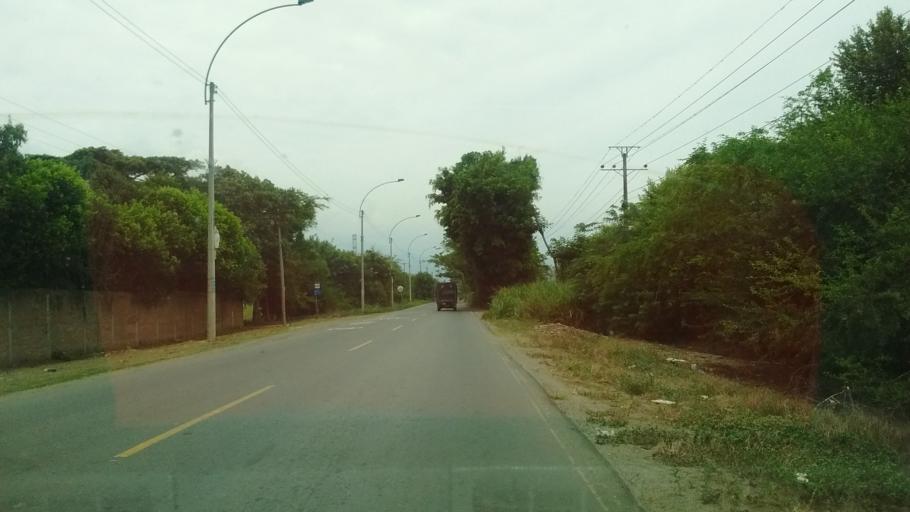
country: CO
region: Valle del Cauca
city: Jamundi
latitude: 3.3306
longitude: -76.5083
